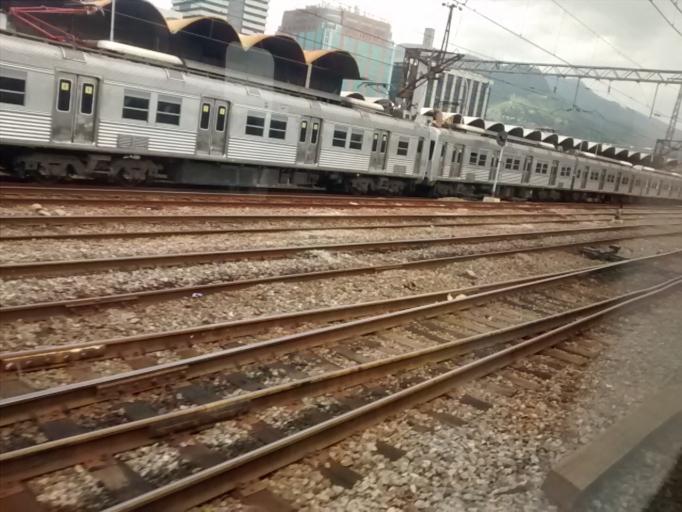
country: BR
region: Rio de Janeiro
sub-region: Rio De Janeiro
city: Rio de Janeiro
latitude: -22.9067
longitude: -43.2033
